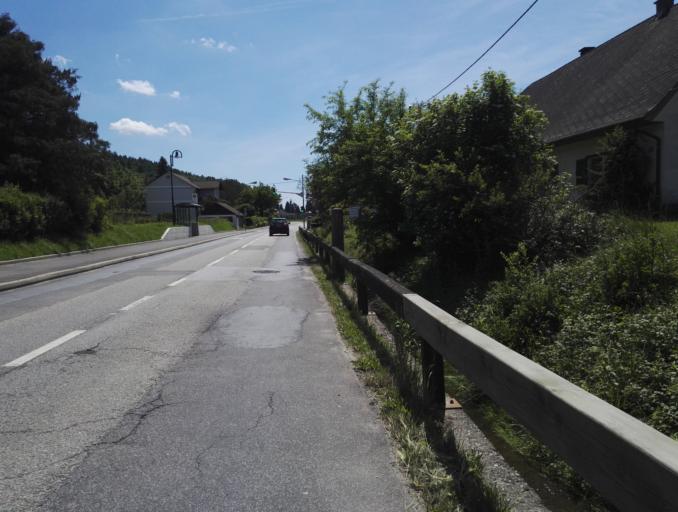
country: AT
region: Styria
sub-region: Politischer Bezirk Graz-Umgebung
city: Grambach
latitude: 47.0116
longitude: 15.5026
